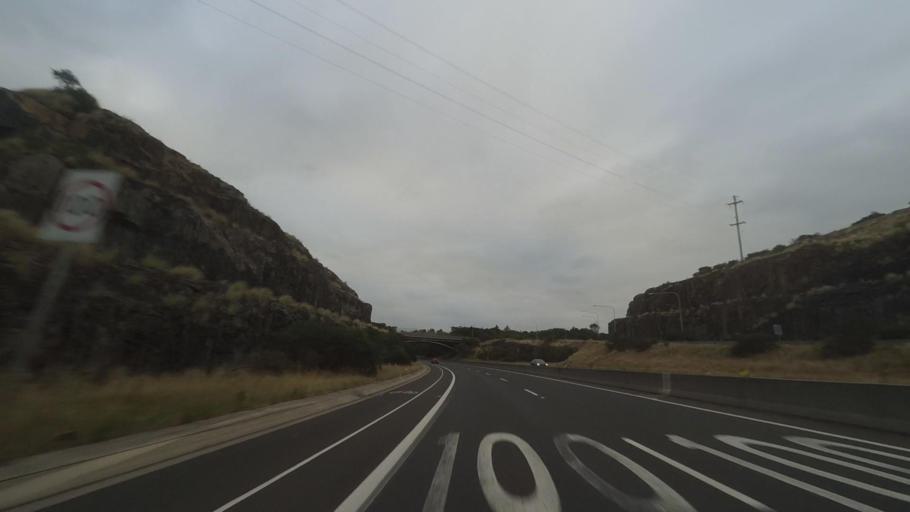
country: AU
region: New South Wales
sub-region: Kiama
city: Kiama
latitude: -34.6511
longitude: 150.8535
